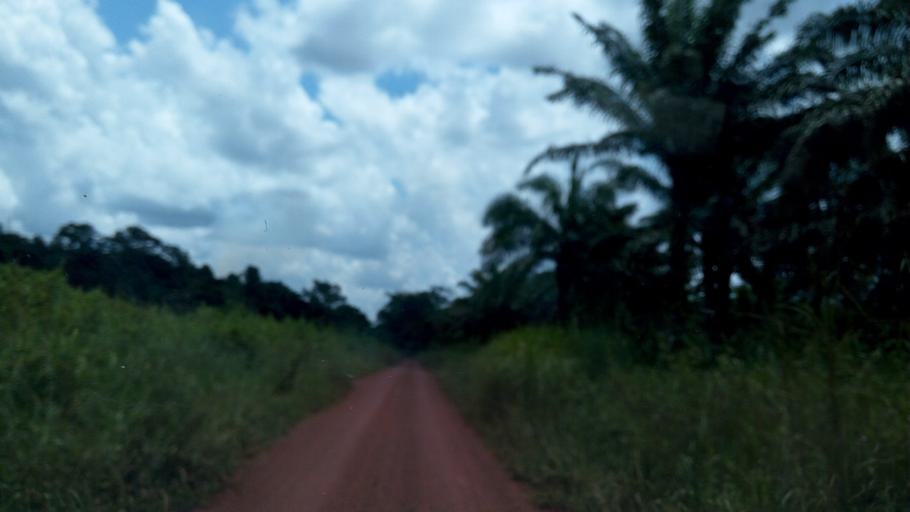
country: CD
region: Equateur
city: Libenge
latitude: 3.7708
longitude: 18.9566
